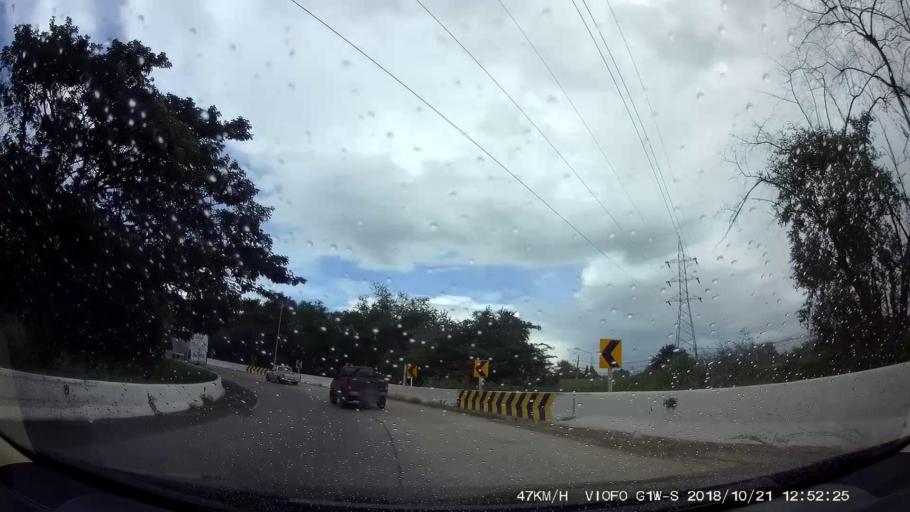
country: TH
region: Nakhon Ratchasima
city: Sikhio
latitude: 14.8618
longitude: 101.7001
